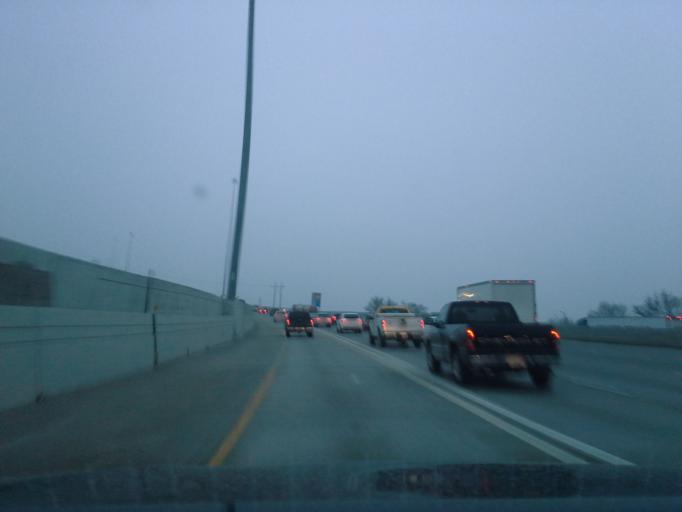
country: US
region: Utah
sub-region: Salt Lake County
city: Midvale
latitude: 40.6349
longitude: -111.9051
